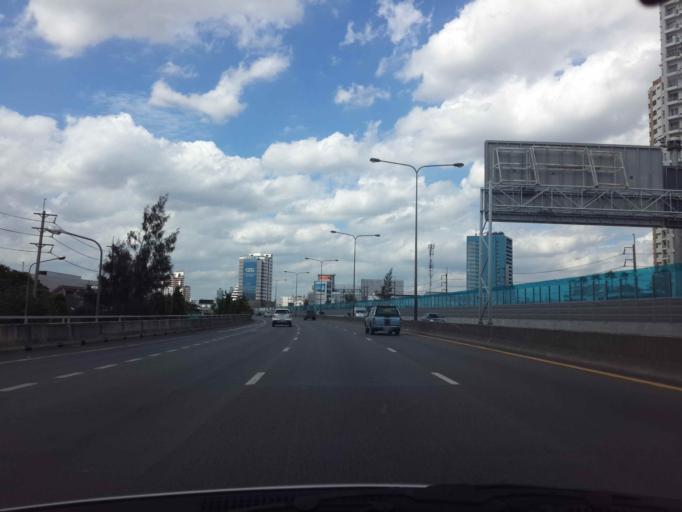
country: TH
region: Bangkok
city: Yan Nawa
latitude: 13.6982
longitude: 100.5400
